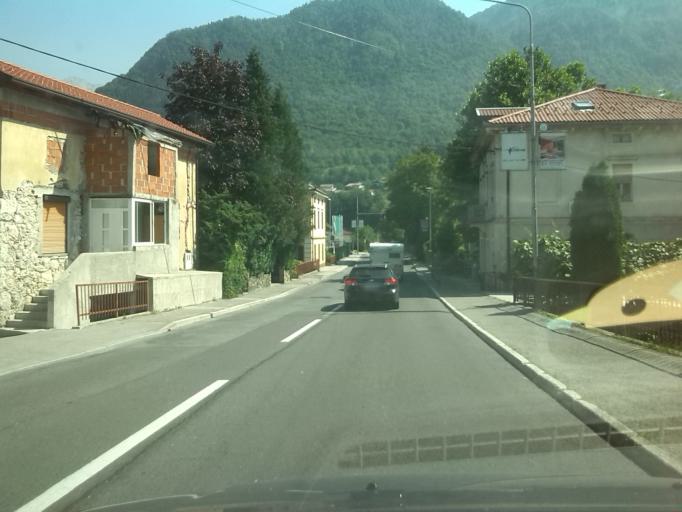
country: SI
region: Tolmin
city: Tolmin
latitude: 46.1835
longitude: 13.7363
